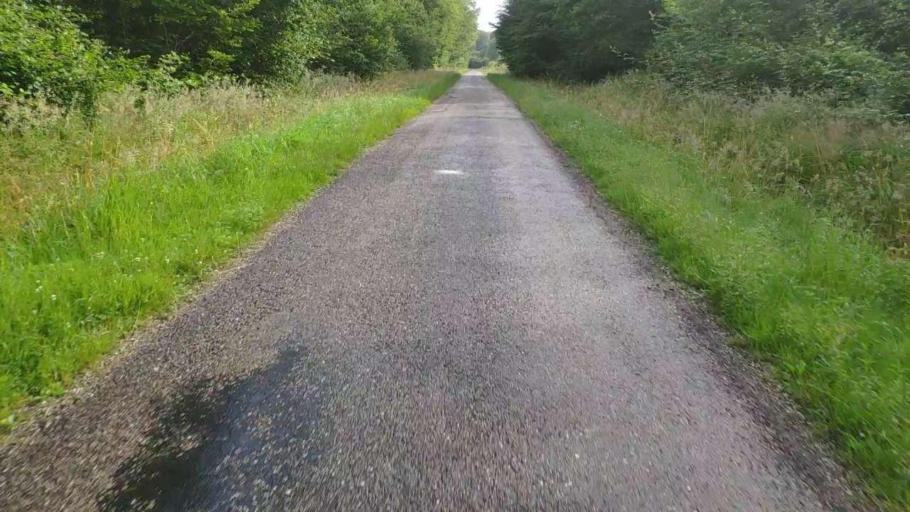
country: FR
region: Franche-Comte
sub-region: Departement du Jura
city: Mont-sous-Vaudrey
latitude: 46.8831
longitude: 5.5242
